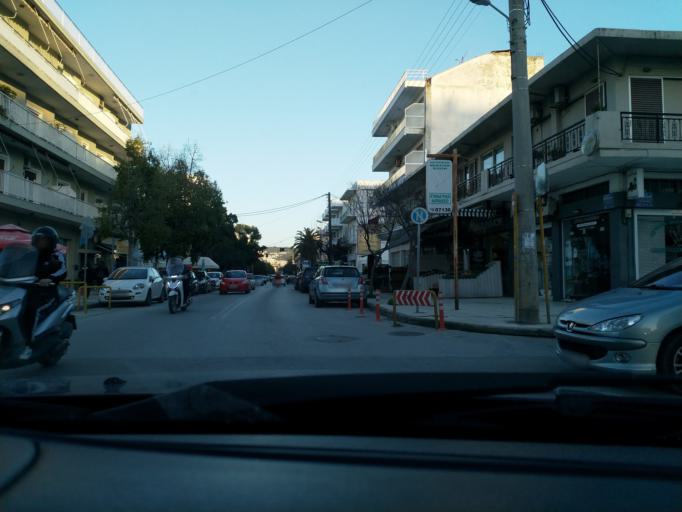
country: GR
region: Crete
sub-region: Nomos Chanias
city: Chania
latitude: 35.5103
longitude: 24.0163
